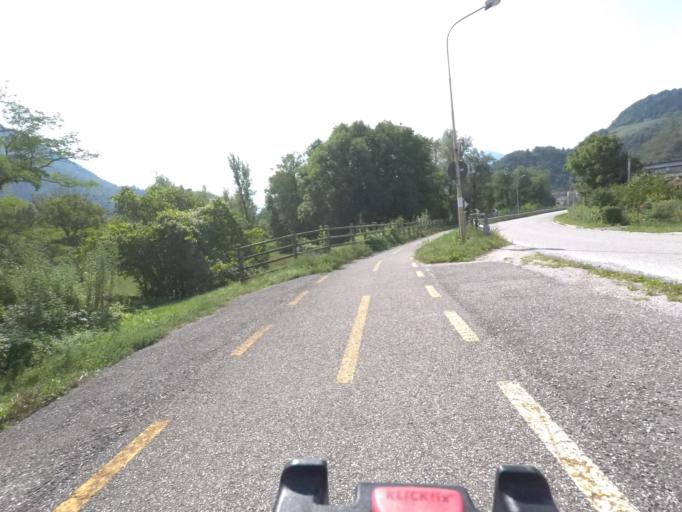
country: IT
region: Friuli Venezia Giulia
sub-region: Provincia di Udine
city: Tolmezzo
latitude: 46.4231
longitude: 13.0120
